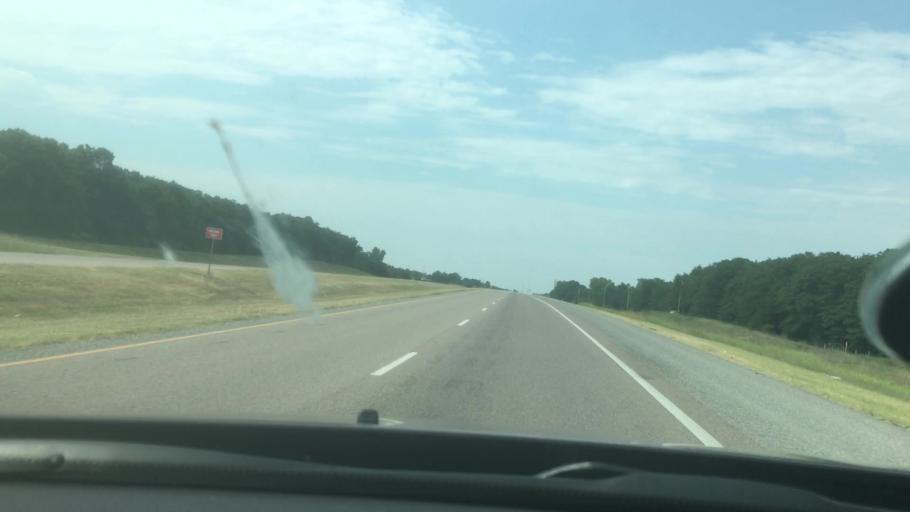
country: US
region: Oklahoma
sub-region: Pontotoc County
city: Byng
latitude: 34.8472
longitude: -96.6839
